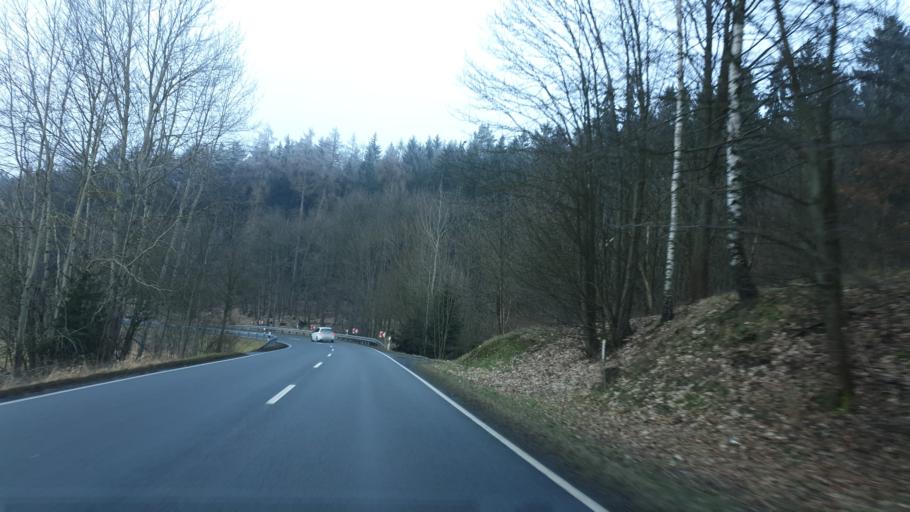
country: DE
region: Saxony
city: Bad Brambach
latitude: 50.2364
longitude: 12.3061
